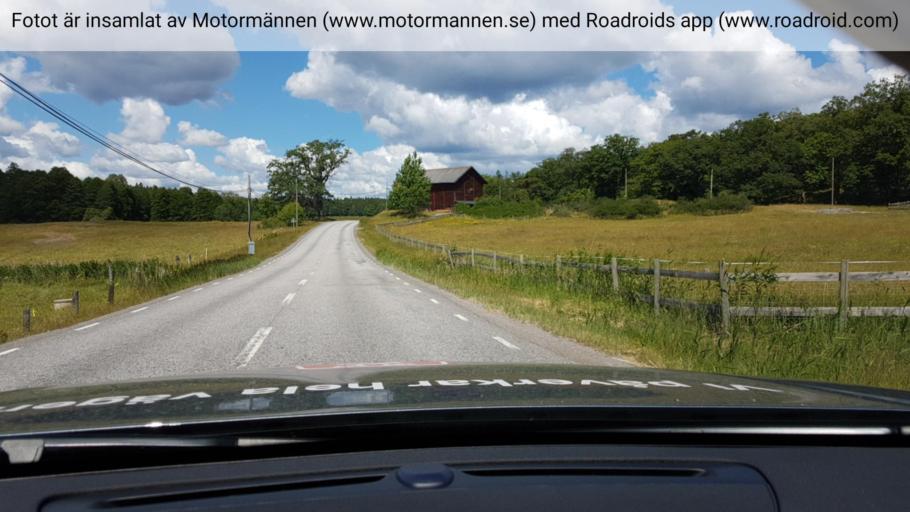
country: SE
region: Stockholm
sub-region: Varmdo Kommun
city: Hemmesta
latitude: 59.3725
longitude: 18.5278
